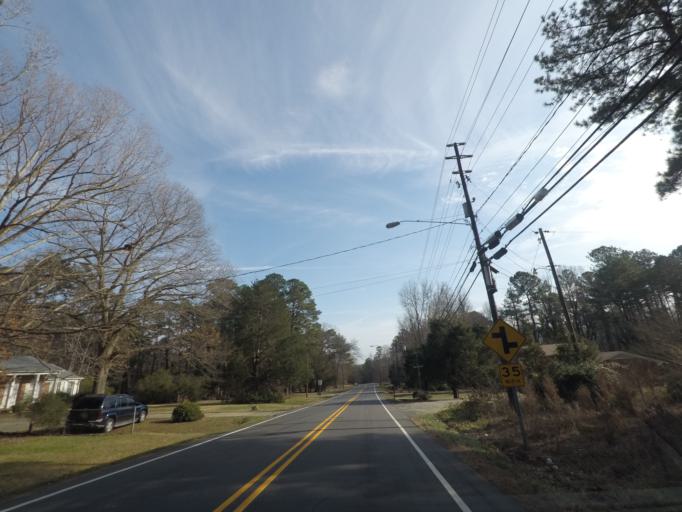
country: US
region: North Carolina
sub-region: Durham County
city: Durham
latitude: 36.0791
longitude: -78.9250
